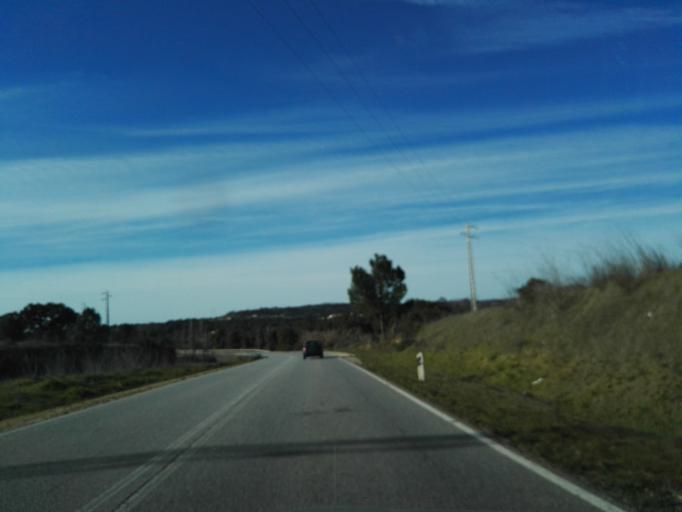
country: PT
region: Santarem
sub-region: Abrantes
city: Alferrarede
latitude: 39.4681
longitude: -8.0600
